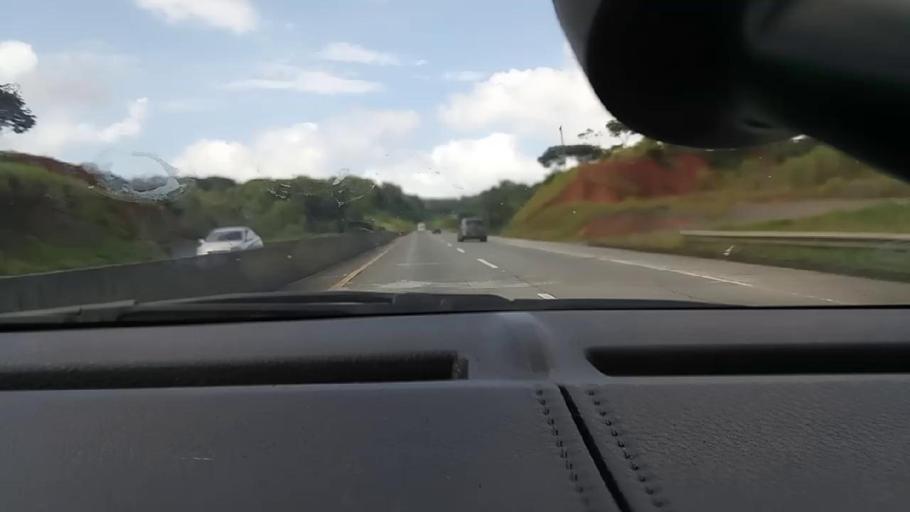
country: PA
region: Colon
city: Gatun
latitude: 9.2823
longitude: -79.7689
